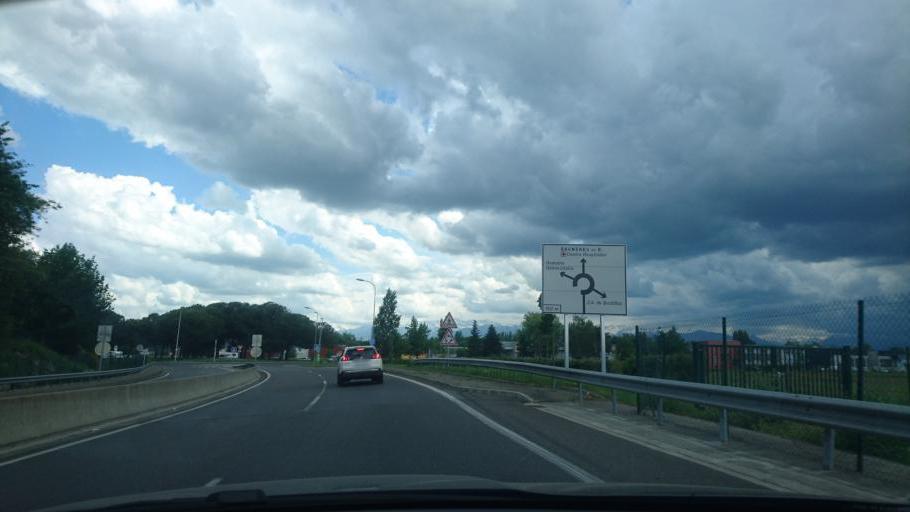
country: FR
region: Midi-Pyrenees
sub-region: Departement des Hautes-Pyrenees
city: Odos
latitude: 43.2243
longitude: 0.0454
